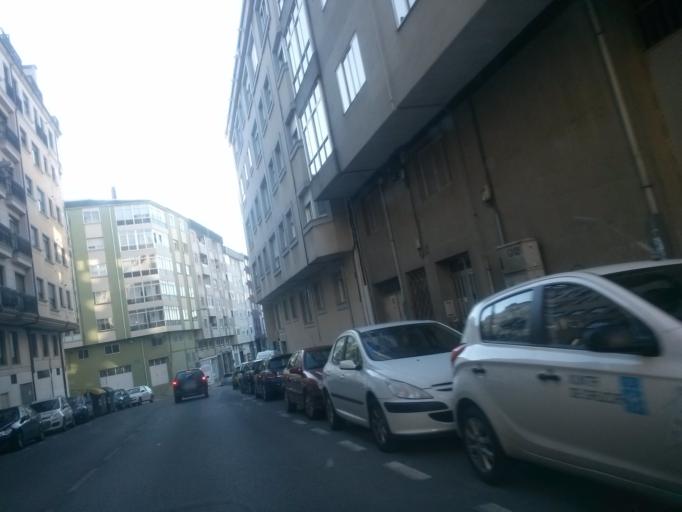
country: ES
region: Galicia
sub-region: Provincia de Lugo
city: Lugo
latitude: 43.0046
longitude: -7.5496
